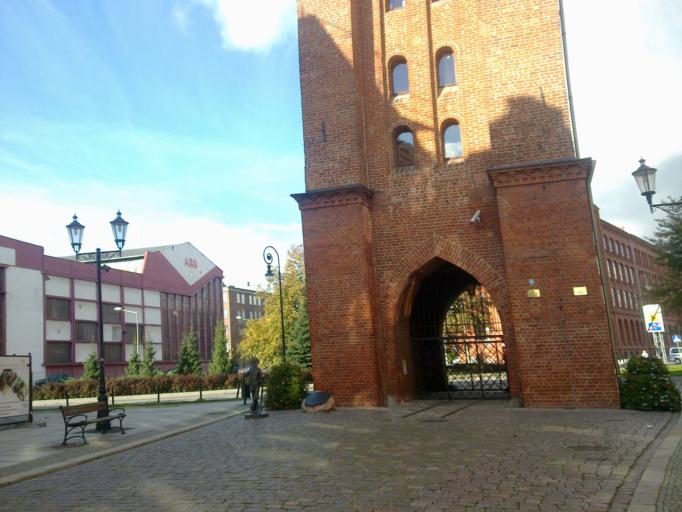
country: PL
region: Warmian-Masurian Voivodeship
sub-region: Powiat elblaski
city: Elblag
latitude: 54.1612
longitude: 19.3956
